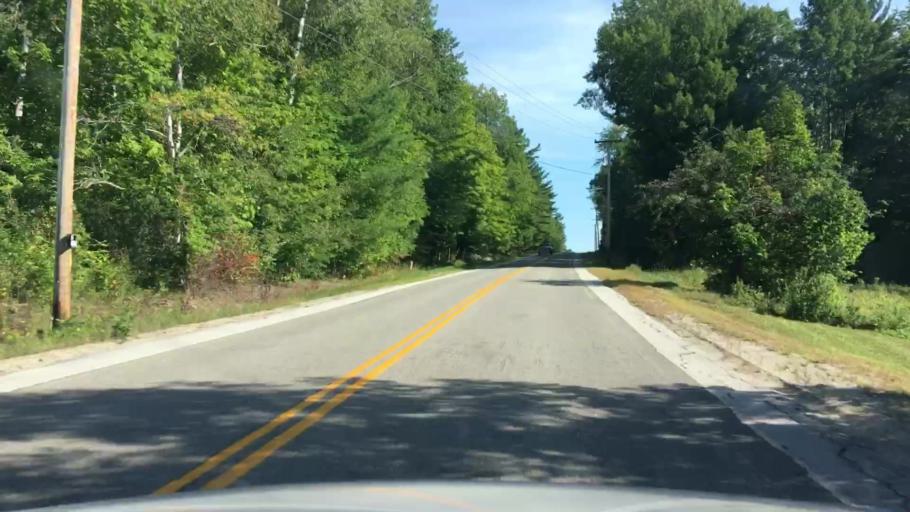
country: US
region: Maine
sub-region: Penobscot County
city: Enfield
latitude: 45.2131
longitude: -68.5259
